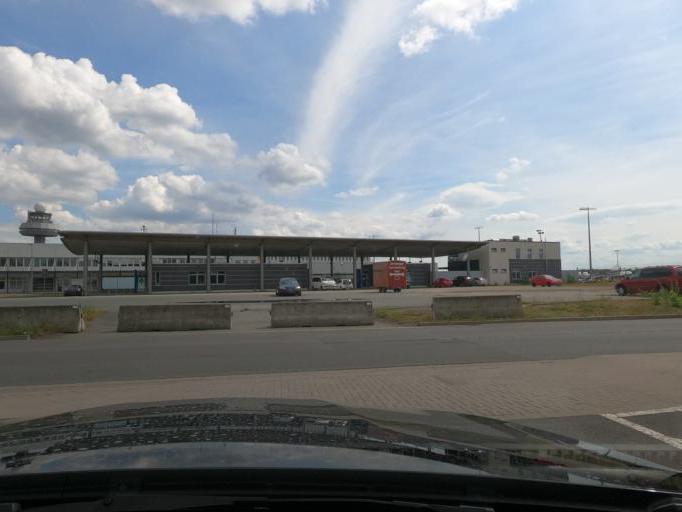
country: DE
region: Lower Saxony
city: Langenhagen
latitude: 52.4621
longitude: 9.6913
